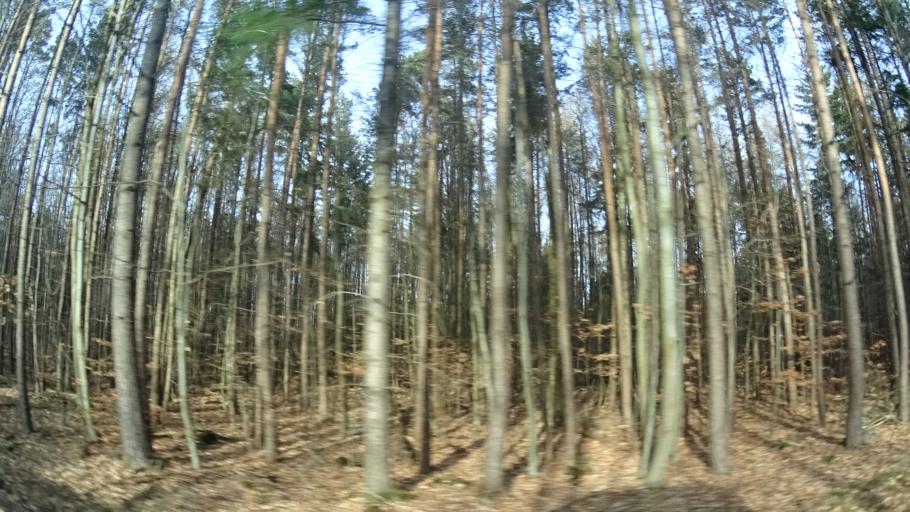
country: DE
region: Bavaria
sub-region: Regierungsbezirk Unterfranken
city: Bad Bocklet
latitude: 50.3408
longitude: 10.0939
